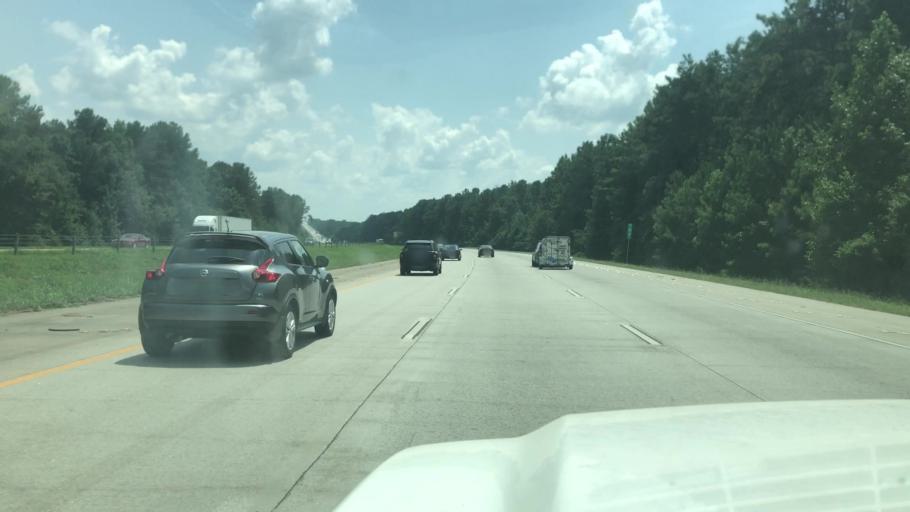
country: US
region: Georgia
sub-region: Coweta County
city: Grantville
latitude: 33.2682
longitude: -84.8045
